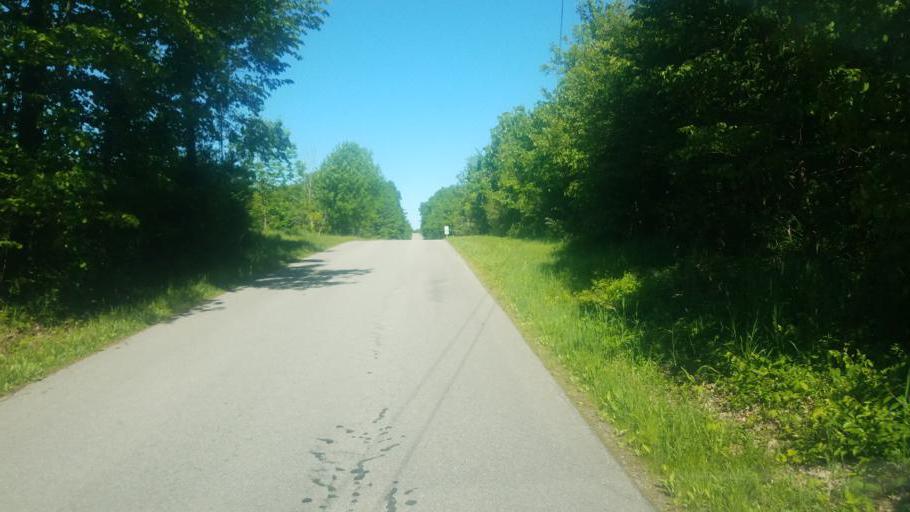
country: US
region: Ohio
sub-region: Logan County
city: Northwood
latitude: 40.4369
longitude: -83.7271
